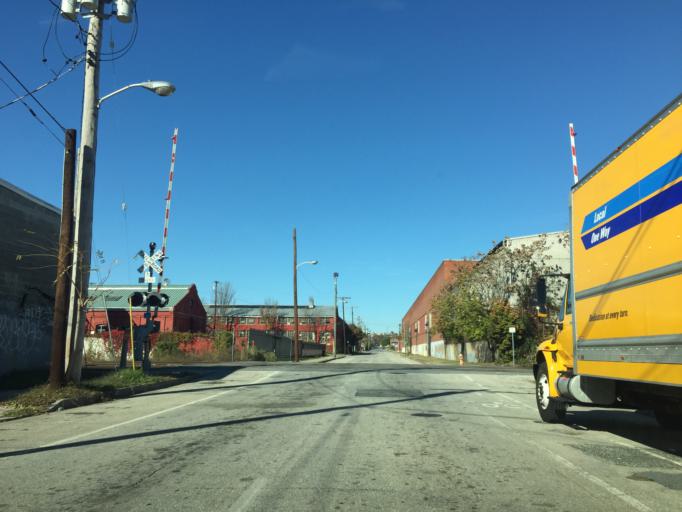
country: US
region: Maryland
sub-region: City of Baltimore
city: Baltimore
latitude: 39.2751
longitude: -76.6308
